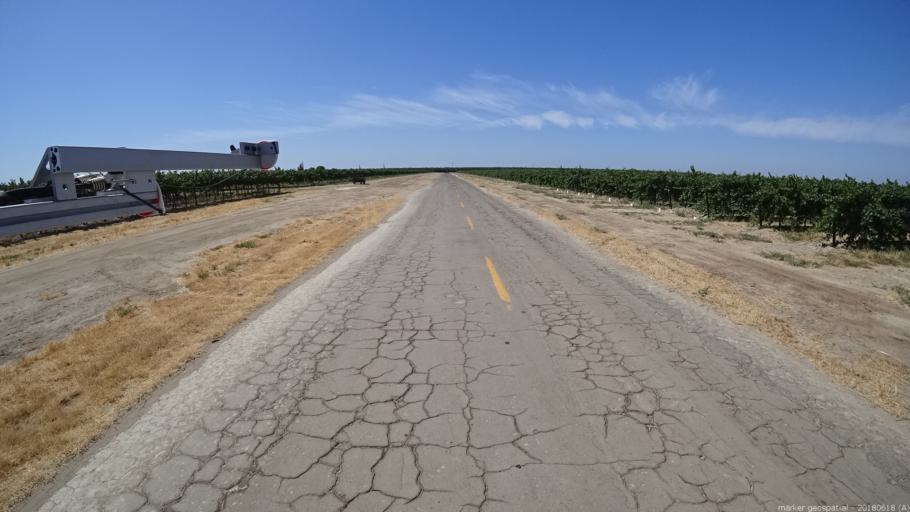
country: US
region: California
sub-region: Madera County
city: Parkwood
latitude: 36.8408
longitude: -120.1828
